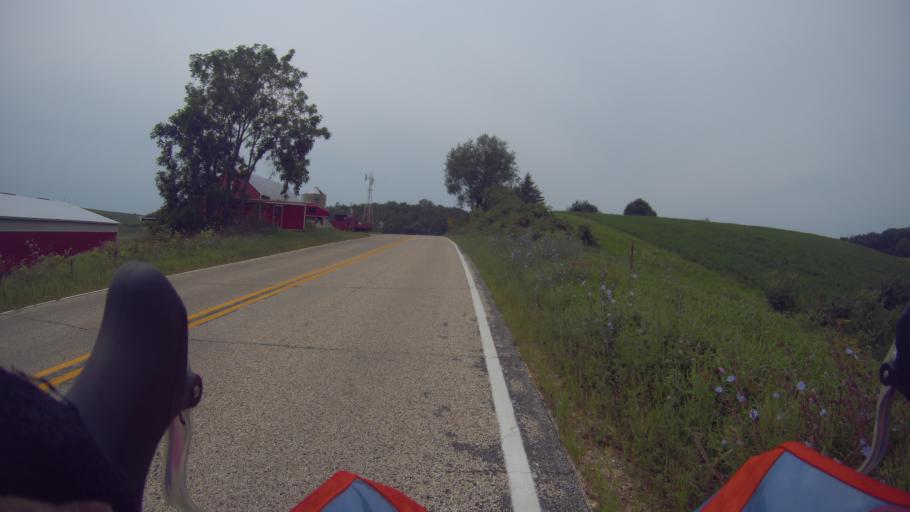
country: US
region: Wisconsin
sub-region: Dane County
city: Mount Horeb
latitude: 42.9208
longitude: -89.6881
